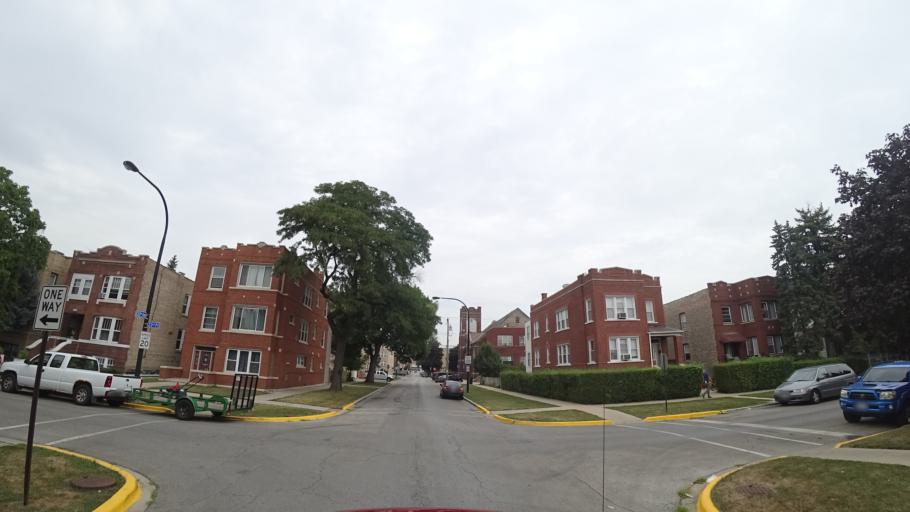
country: US
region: Illinois
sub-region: Cook County
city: Cicero
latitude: 41.8482
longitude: -87.7565
